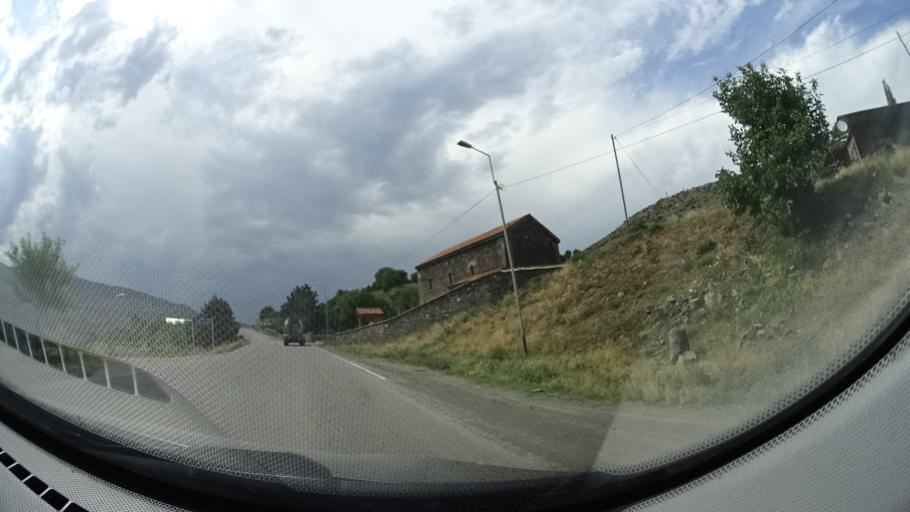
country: GE
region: Samtskhe-Javakheti
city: Aspindza
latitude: 41.5648
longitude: 43.2628
